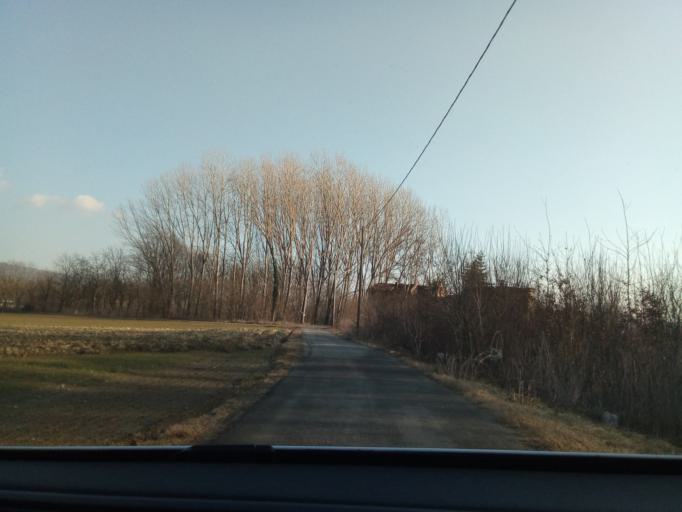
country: IT
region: Piedmont
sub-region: Provincia di Torino
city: Cascinette d'Ivrea
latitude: 45.4608
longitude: 7.9176
